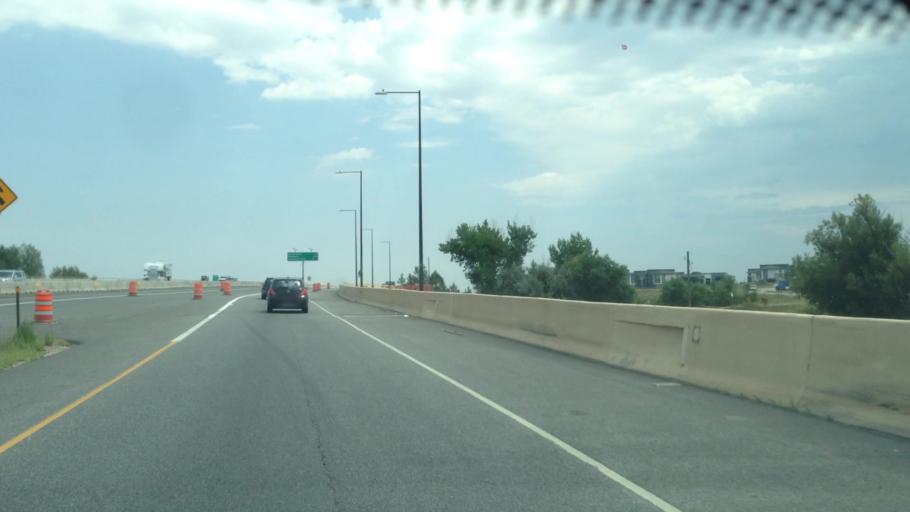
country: US
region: Colorado
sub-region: Arapahoe County
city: Columbine Valley
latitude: 39.5636
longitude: -105.0243
